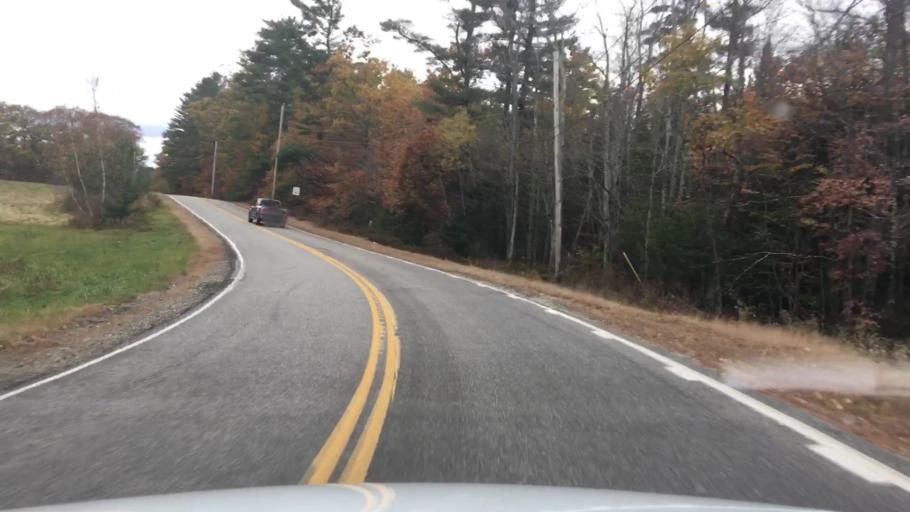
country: US
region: Maine
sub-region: Sagadahoc County
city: Richmond
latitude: 44.1271
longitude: -69.9038
